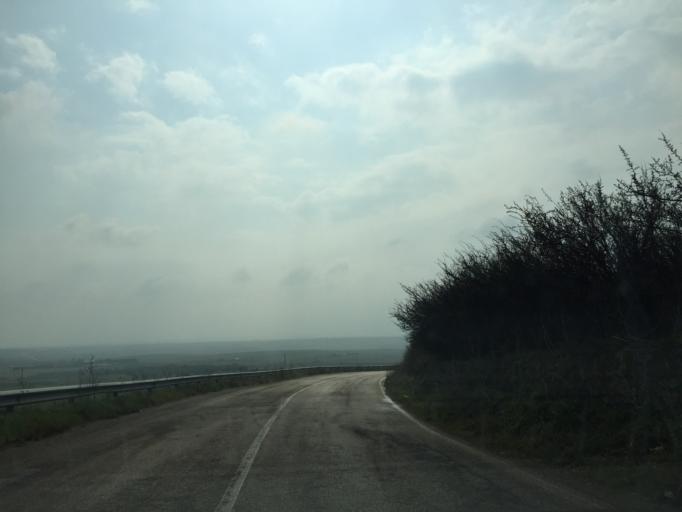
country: IT
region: Apulia
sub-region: Provincia di Foggia
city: Troia
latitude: 41.3636
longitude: 15.3238
